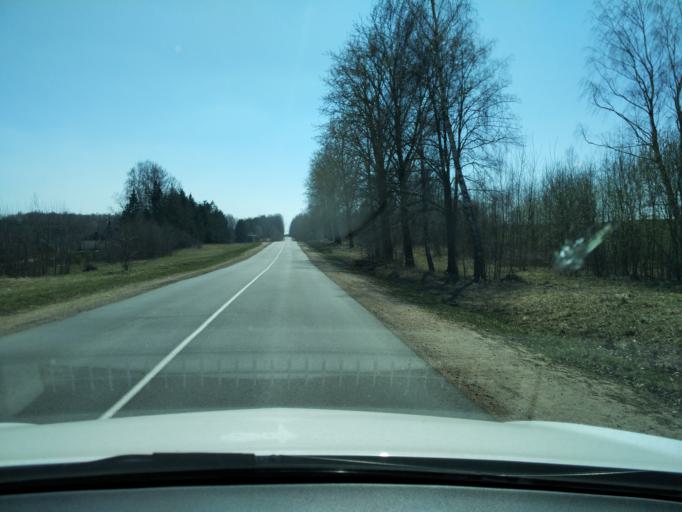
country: BY
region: Minsk
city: Slabada
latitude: 53.9834
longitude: 27.9561
